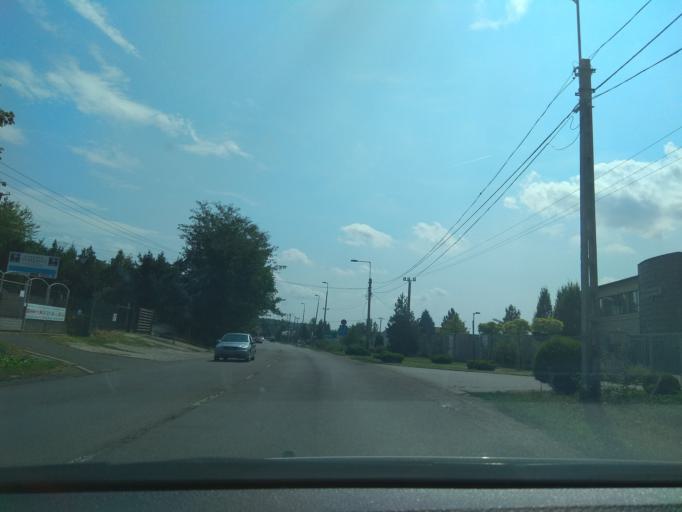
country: HU
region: Heves
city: Andornaktalya
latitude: 47.8743
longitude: 20.4017
